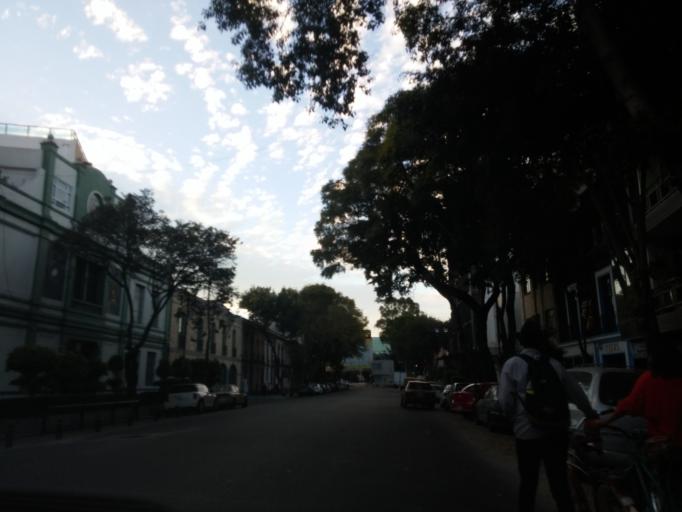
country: MX
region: Mexico City
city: Cuauhtemoc
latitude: 19.4372
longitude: -99.1581
